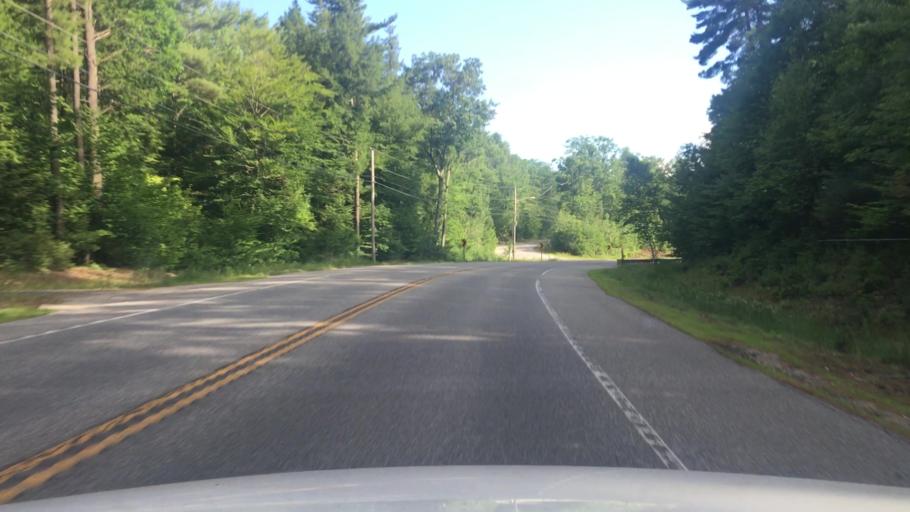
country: US
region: Maine
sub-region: Androscoggin County
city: Livermore Falls
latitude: 44.4317
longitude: -70.2124
